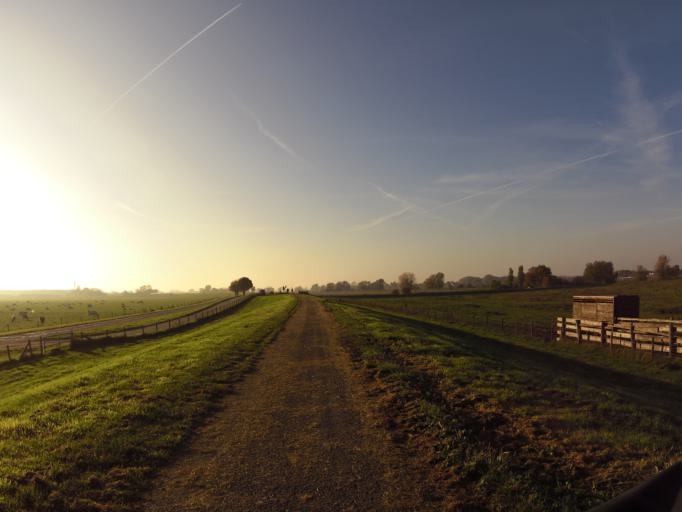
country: NL
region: Gelderland
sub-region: Gemeente Maasdriel
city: Hedel
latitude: 51.7403
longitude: 5.2233
